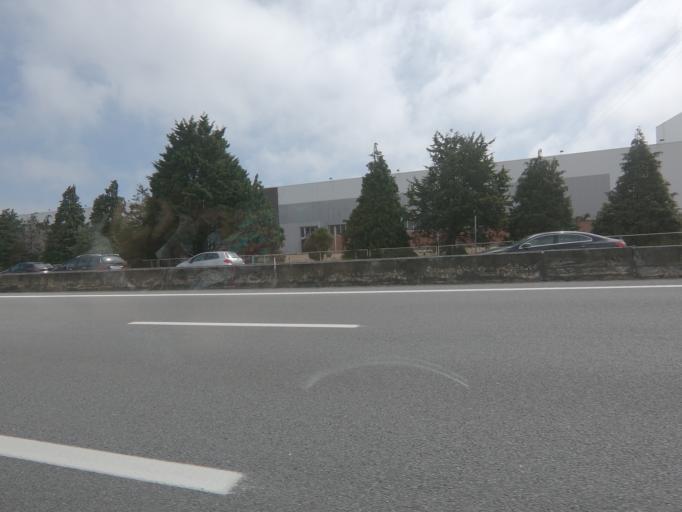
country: PT
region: Porto
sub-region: Matosinhos
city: Santa Cruz do Bispo
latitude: 41.2146
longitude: -8.6907
